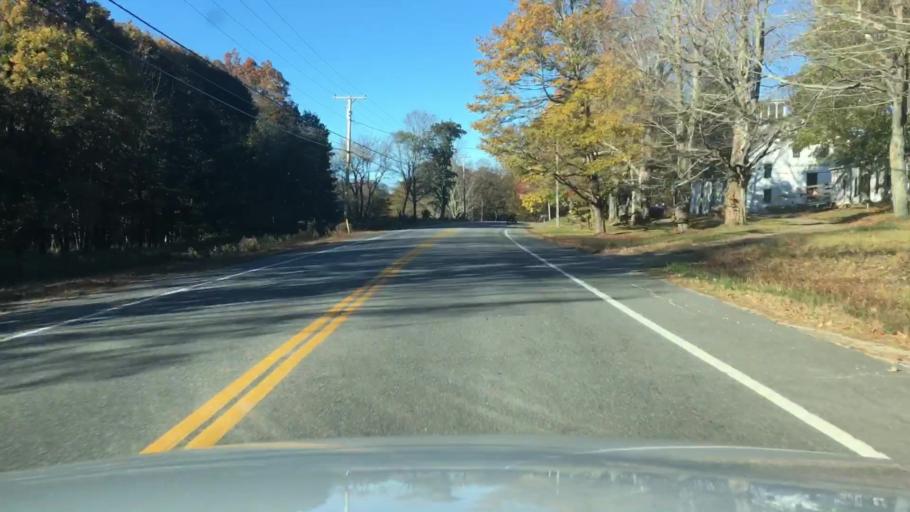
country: US
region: Maine
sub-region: Sagadahoc County
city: Topsham
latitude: 44.0479
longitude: -69.9401
